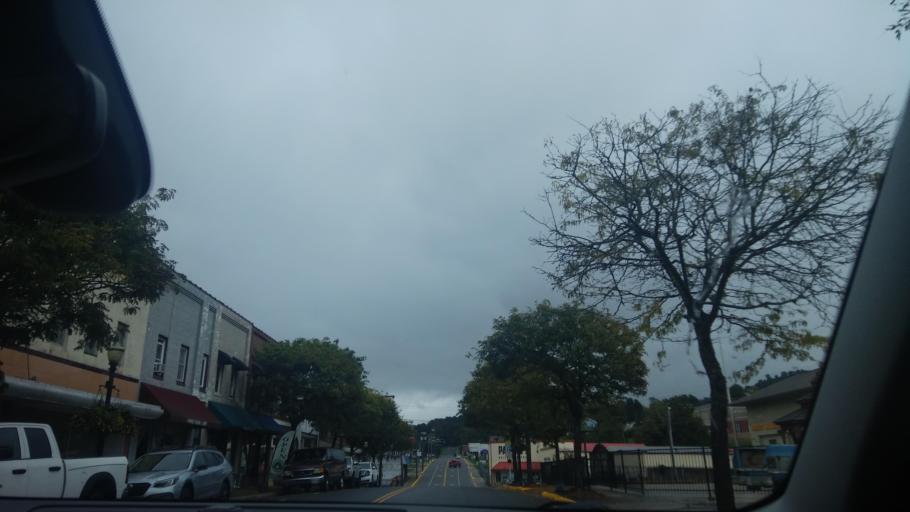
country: US
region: Virginia
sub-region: City of Galax
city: Galax
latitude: 36.6607
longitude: -80.9243
